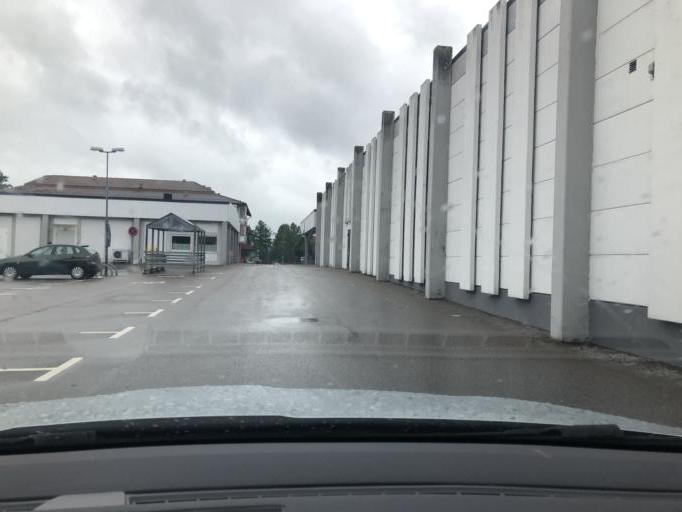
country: SE
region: Blekinge
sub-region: Olofstroms Kommun
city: Olofstroem
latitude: 56.2784
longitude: 14.5322
